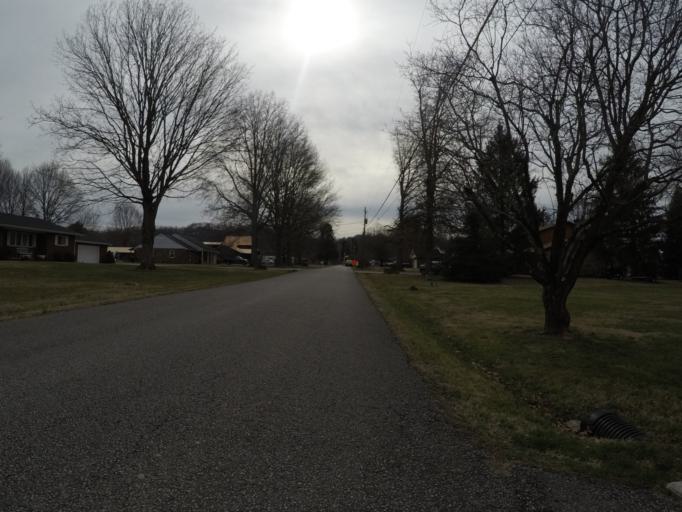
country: US
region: West Virginia
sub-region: Cabell County
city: Pea Ridge
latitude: 38.4461
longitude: -82.3459
